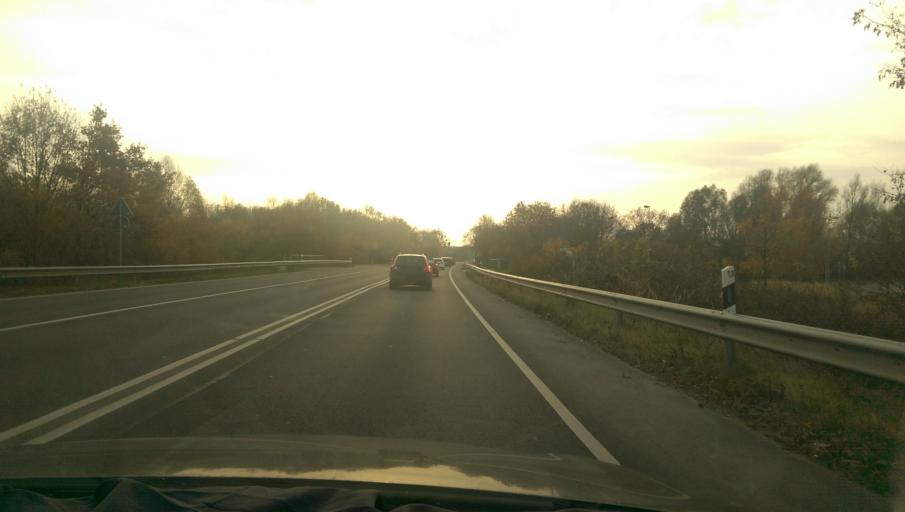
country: DE
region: Lower Saxony
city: Wolfsburg
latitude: 52.4440
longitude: 10.7918
